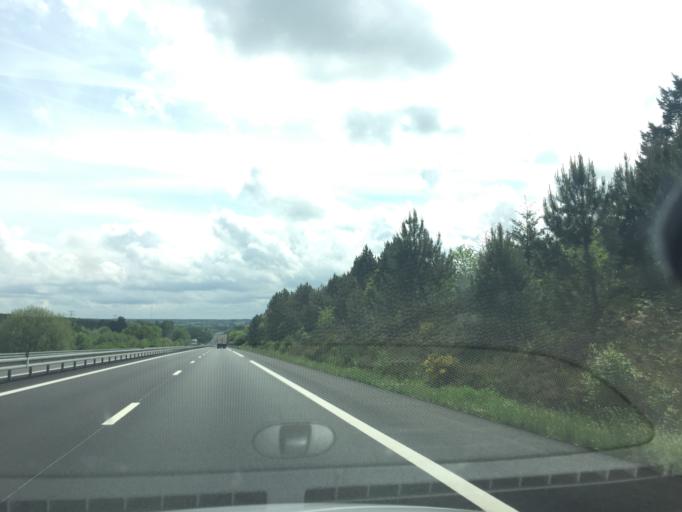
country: FR
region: Pays de la Loire
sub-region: Departement de la Sarthe
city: Ecommoy
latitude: 47.8384
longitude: 0.3055
